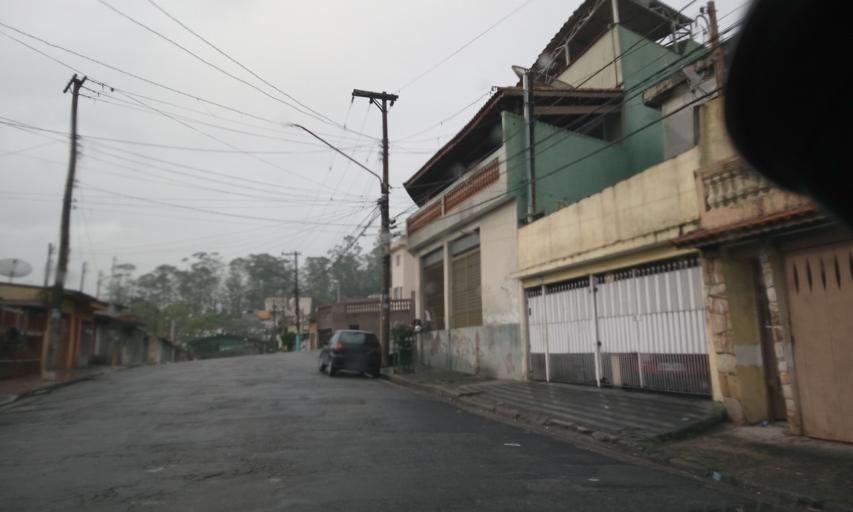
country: BR
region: Sao Paulo
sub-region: Santo Andre
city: Santo Andre
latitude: -23.7114
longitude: -46.5022
